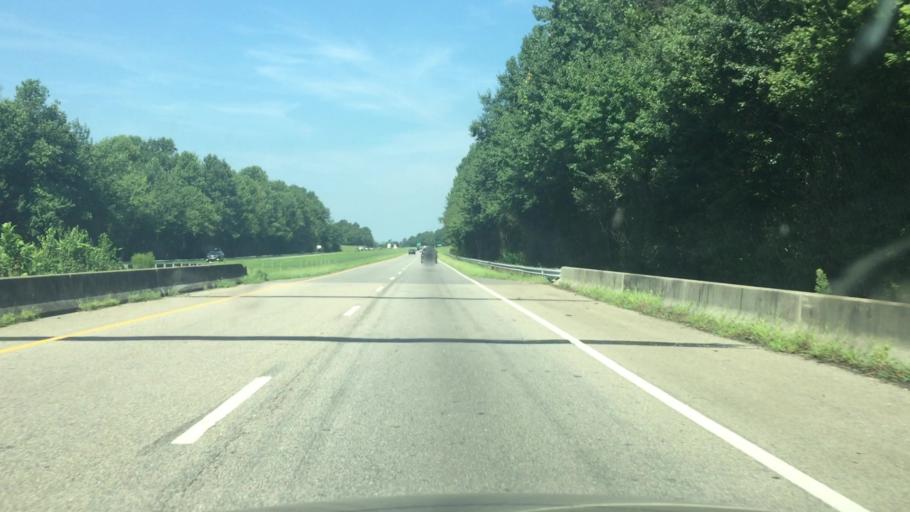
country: US
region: North Carolina
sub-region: Robeson County
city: Maxton
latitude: 34.7617
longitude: -79.3858
